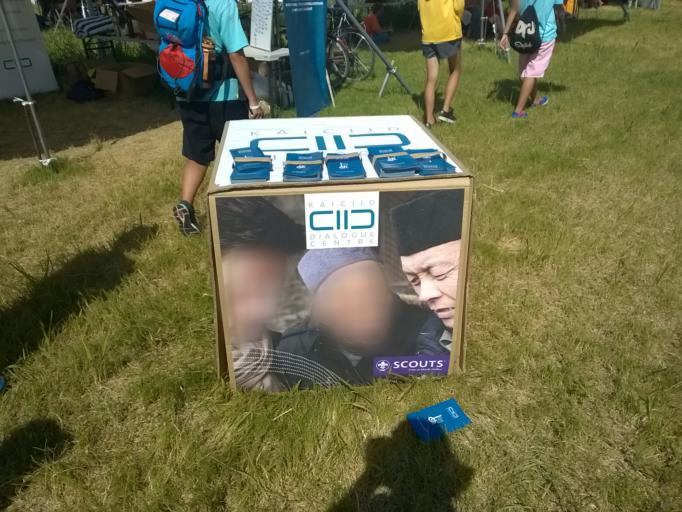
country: JP
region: Yamaguchi
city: Ogori-shimogo
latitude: 34.0155
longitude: 131.3708
